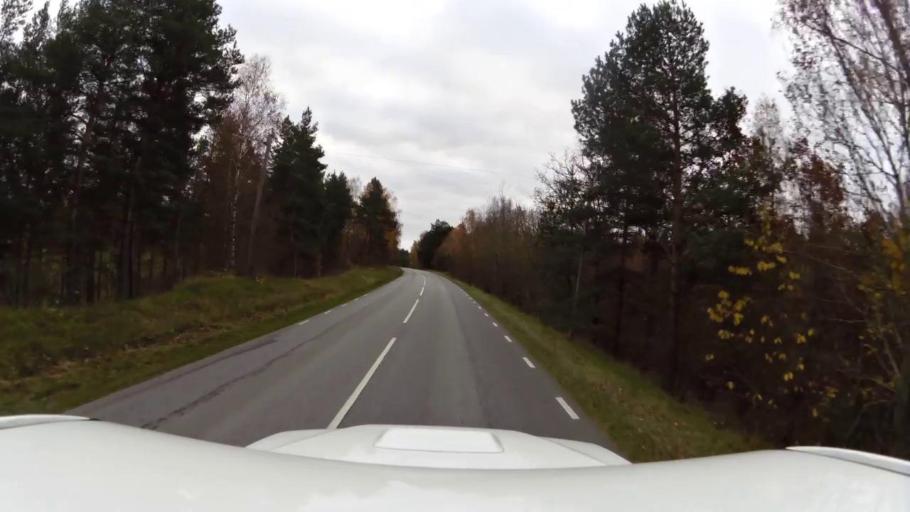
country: SE
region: OEstergoetland
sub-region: Norrkopings Kommun
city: Kimstad
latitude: 58.4022
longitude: 15.9460
